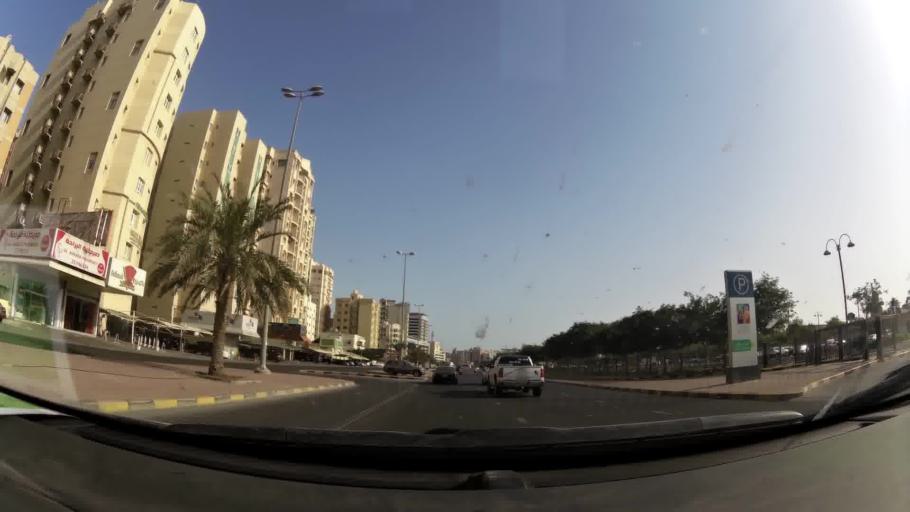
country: KW
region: Muhafazat Hawalli
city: Ar Rumaythiyah
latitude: 29.3203
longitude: 48.0675
